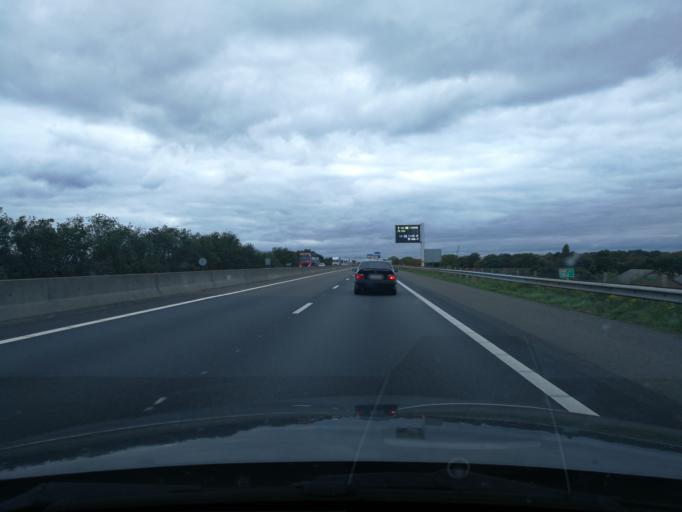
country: NL
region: Limburg
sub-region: Gemeente Venlo
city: Venlo
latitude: 51.3954
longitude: 6.1509
